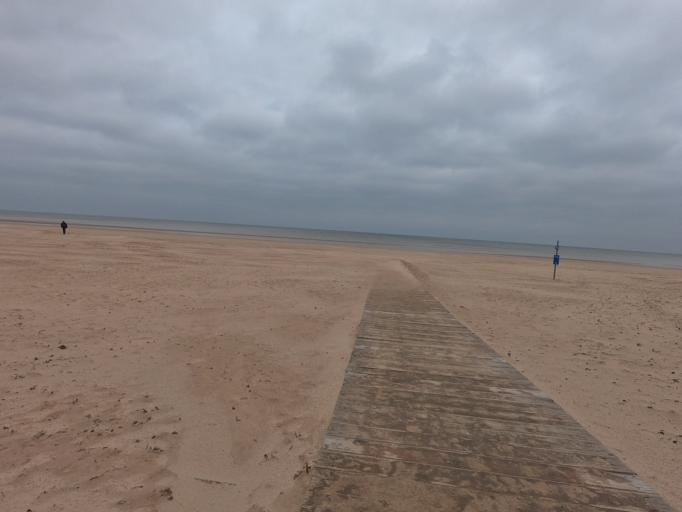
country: LV
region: Riga
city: Bolderaja
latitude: 57.0817
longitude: 24.1075
